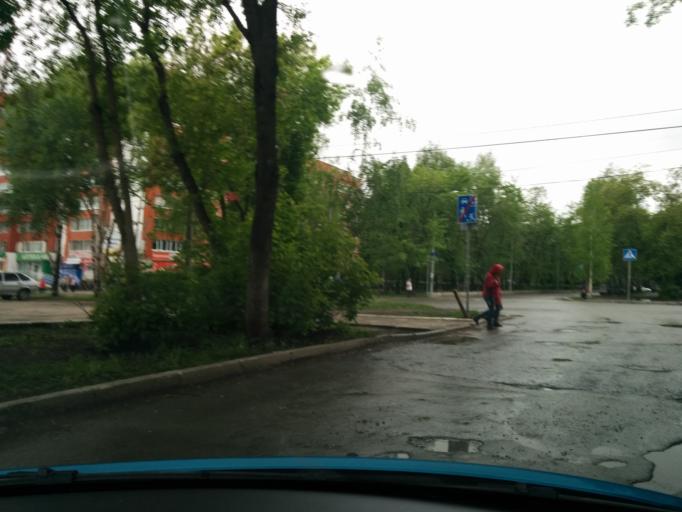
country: RU
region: Perm
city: Perm
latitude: 58.0175
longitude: 56.2929
